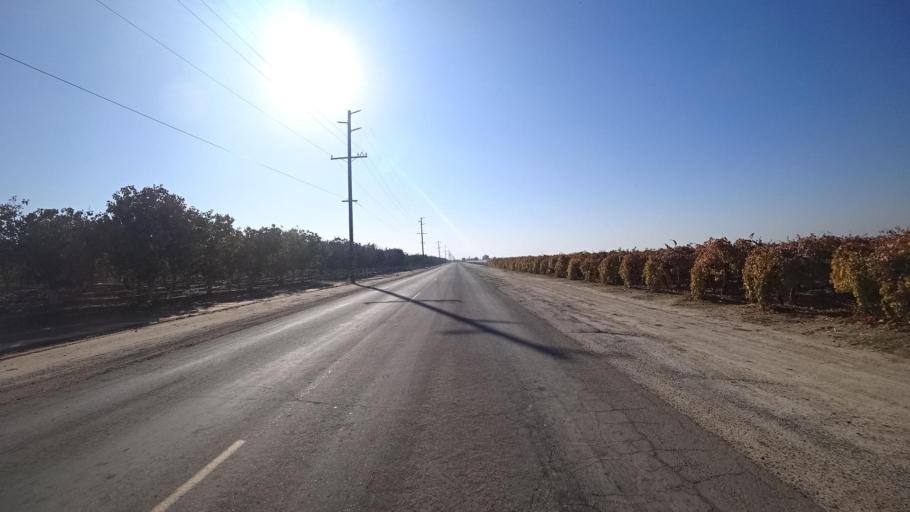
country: US
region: California
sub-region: Kern County
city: McFarland
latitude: 35.7224
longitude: -119.2039
